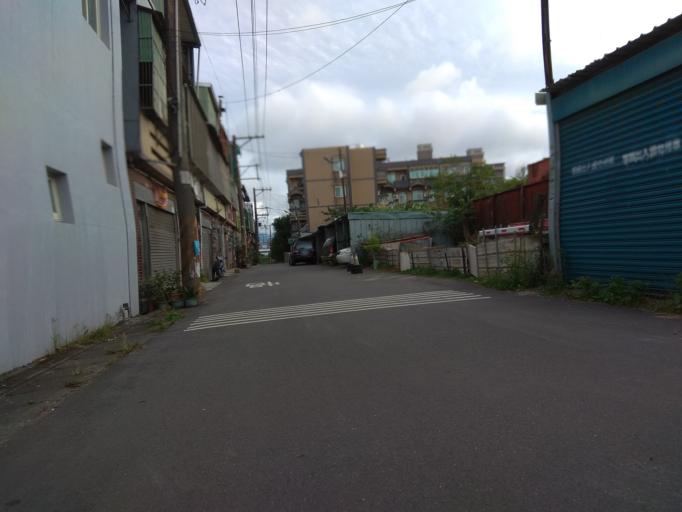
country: TW
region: Taiwan
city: Daxi
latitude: 24.9284
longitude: 121.1956
